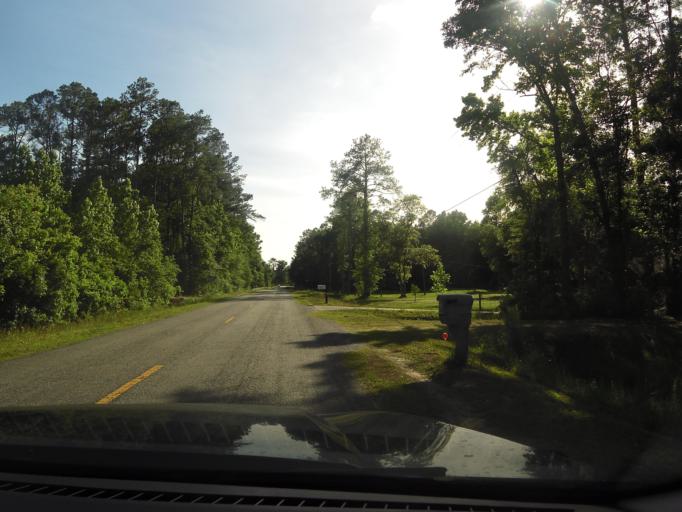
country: US
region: Florida
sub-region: Nassau County
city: Nassau Village-Ratliff
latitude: 30.4845
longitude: -81.8430
